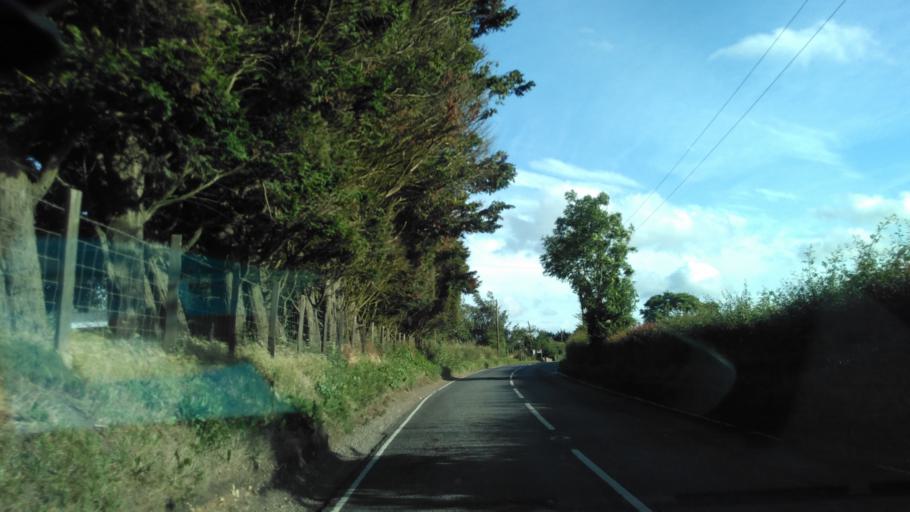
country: GB
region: England
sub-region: Kent
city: Faversham
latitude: 51.2431
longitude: 0.8772
